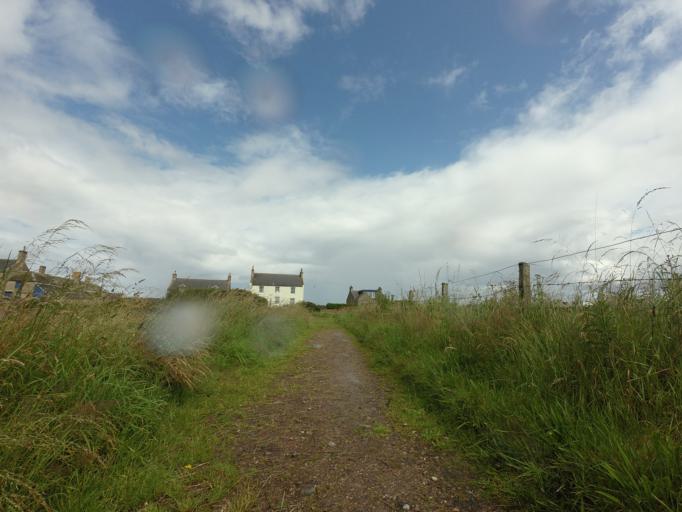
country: GB
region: Scotland
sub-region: Moray
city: Fochabers
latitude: 57.6725
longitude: -3.0919
